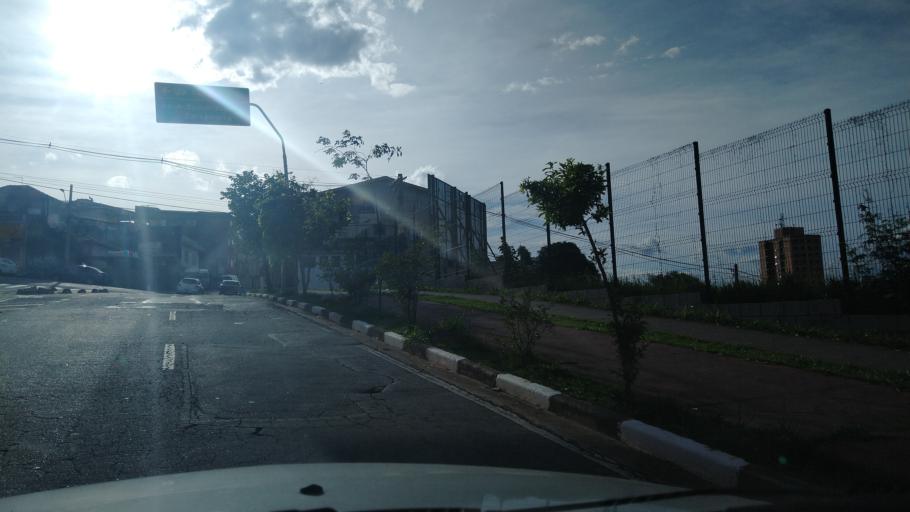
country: BR
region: Sao Paulo
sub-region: Osasco
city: Osasco
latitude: -23.5314
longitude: -46.8102
